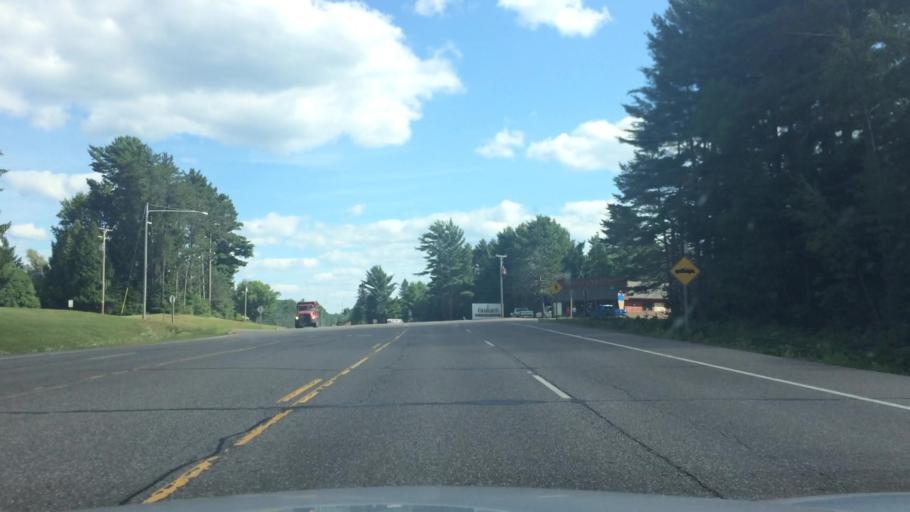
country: US
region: Wisconsin
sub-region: Vilas County
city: Lac du Flambeau
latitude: 45.8090
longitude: -89.7254
